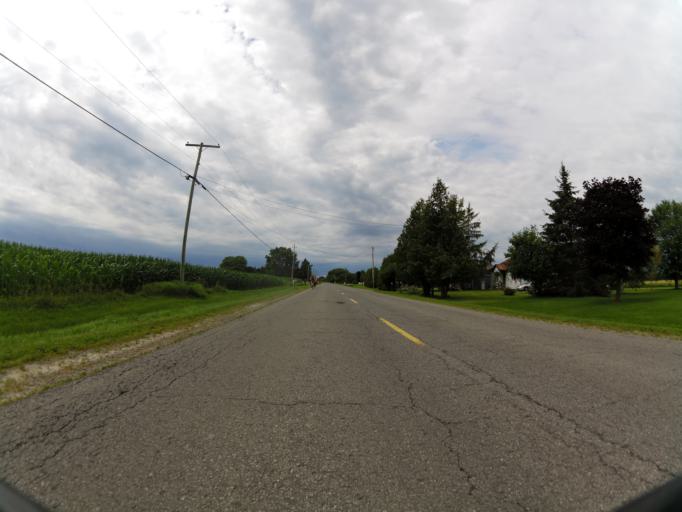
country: CA
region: Ontario
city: Bells Corners
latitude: 45.0191
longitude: -75.7139
